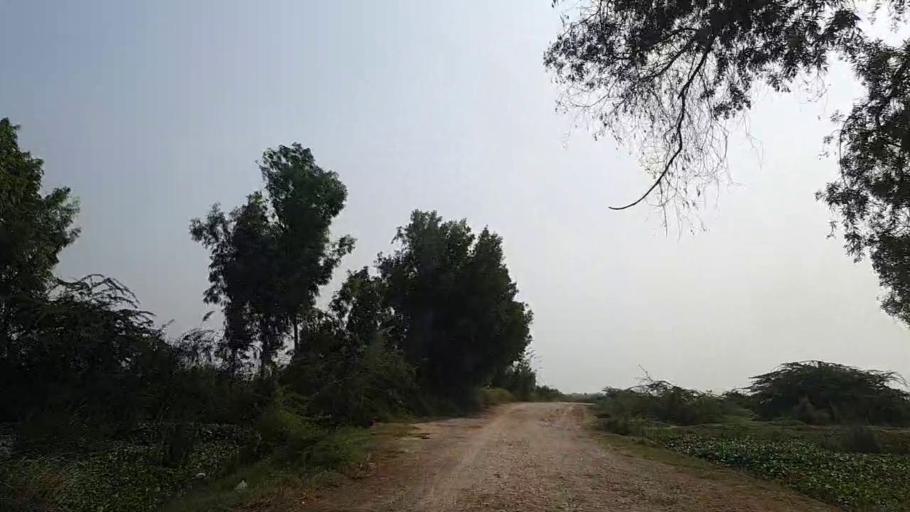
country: PK
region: Sindh
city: Mirpur Sakro
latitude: 24.5919
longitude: 67.7187
